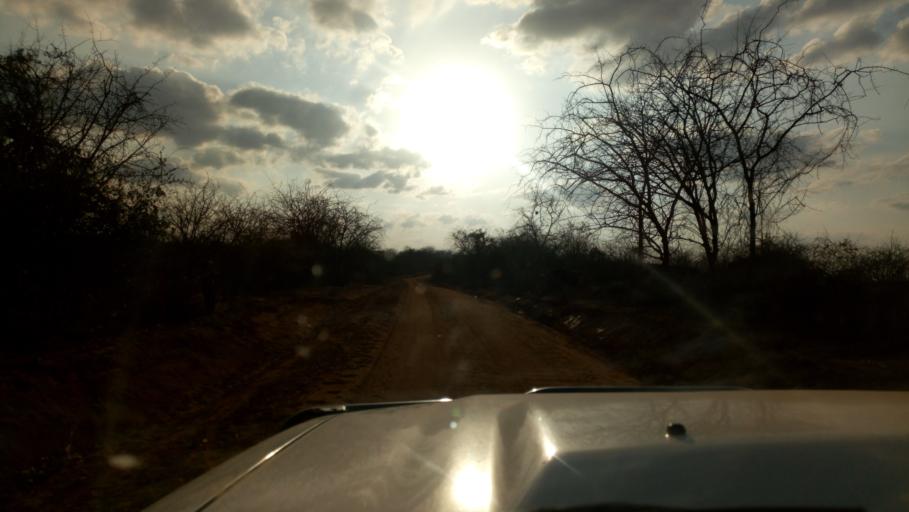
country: KE
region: Kitui
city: Kitui
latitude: -1.6544
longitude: 38.3062
